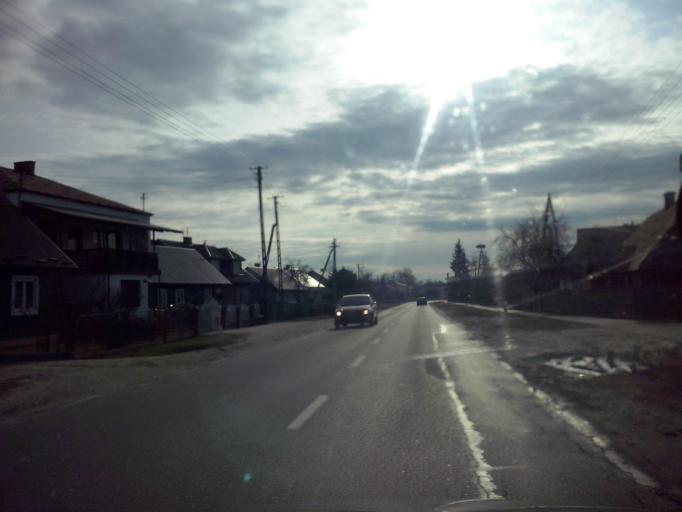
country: PL
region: Lublin Voivodeship
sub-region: Powiat bilgorajski
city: Bilgoraj
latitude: 50.5010
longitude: 22.6446
